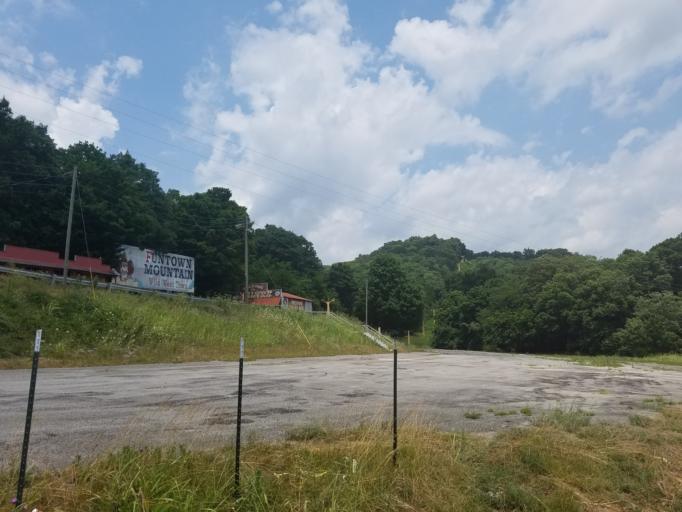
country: US
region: Kentucky
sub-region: Barren County
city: Cave City
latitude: 37.1365
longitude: -85.9794
